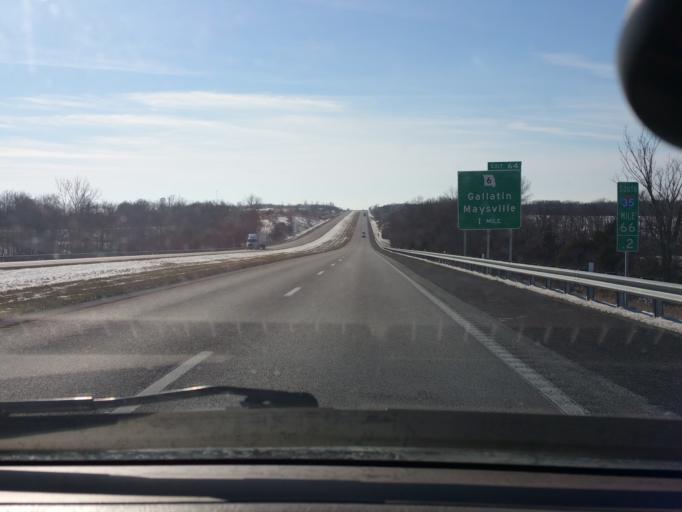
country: US
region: Missouri
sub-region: Daviess County
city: Gallatin
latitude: 39.9167
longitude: -94.1428
